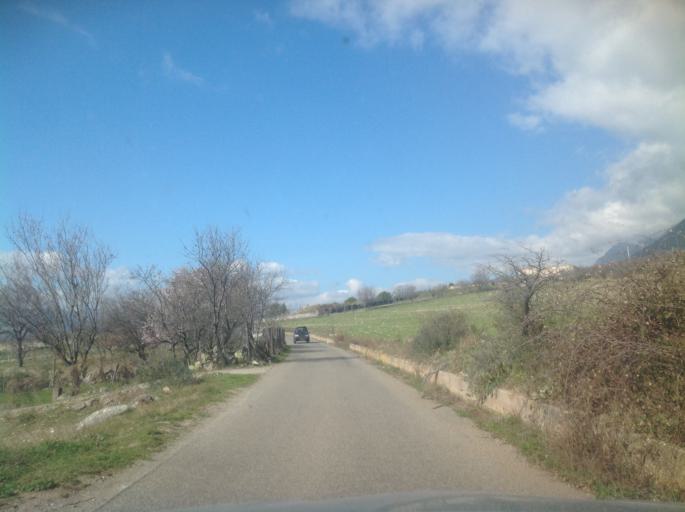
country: IT
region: Calabria
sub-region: Provincia di Cosenza
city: Frascineto
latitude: 39.8383
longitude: 16.2639
